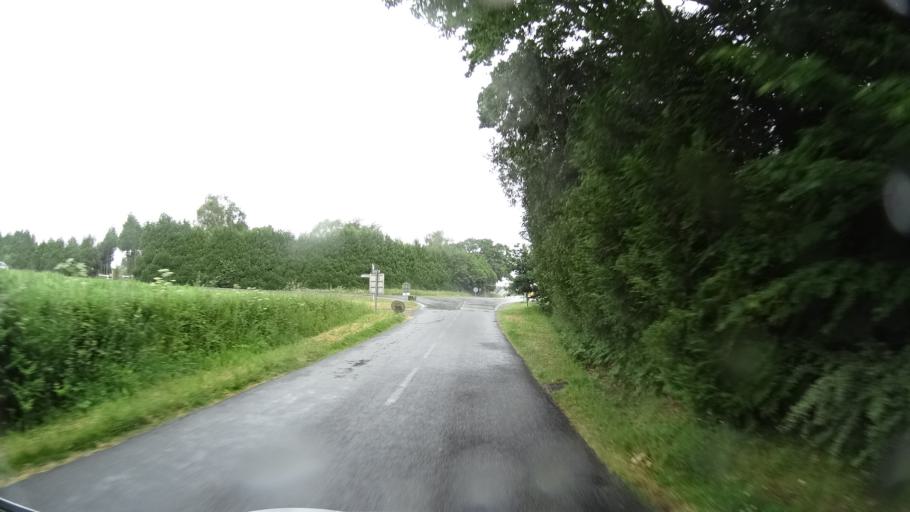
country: FR
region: Brittany
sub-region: Departement d'Ille-et-Vilaine
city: Vern-sur-Seiche
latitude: 48.0445
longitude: -1.6219
